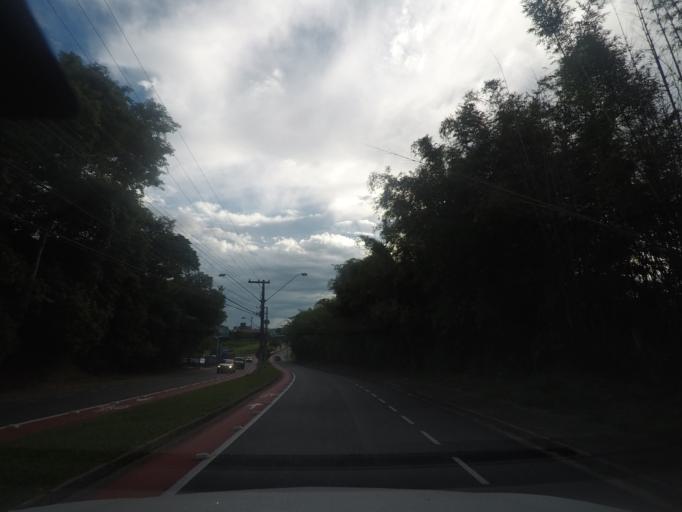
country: BR
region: Sao Paulo
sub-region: Taubate
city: Taubate
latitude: -23.0438
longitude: -45.5936
